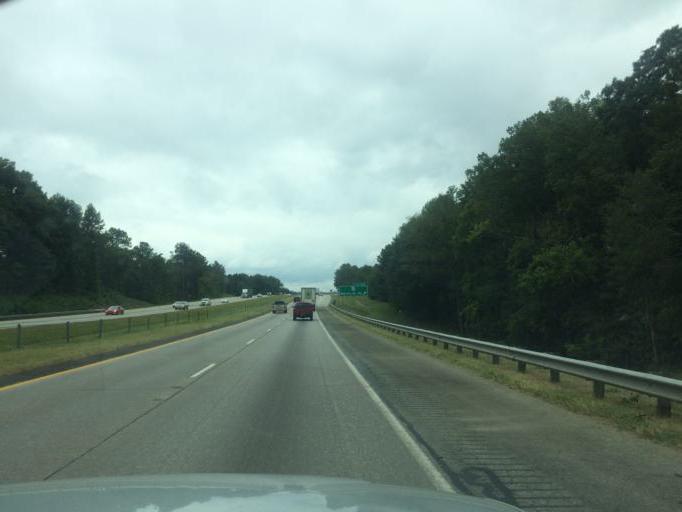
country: US
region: Georgia
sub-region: Banks County
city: Homer
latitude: 34.3018
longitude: -83.3991
